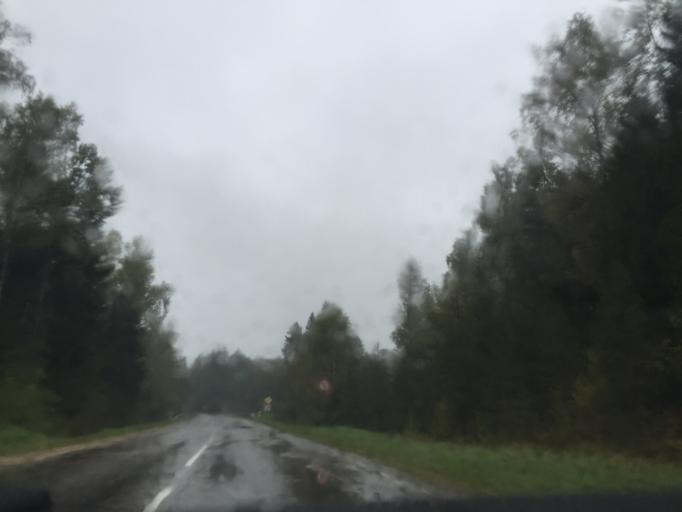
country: LV
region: Ropazu
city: Ropazi
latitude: 57.0124
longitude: 24.6812
